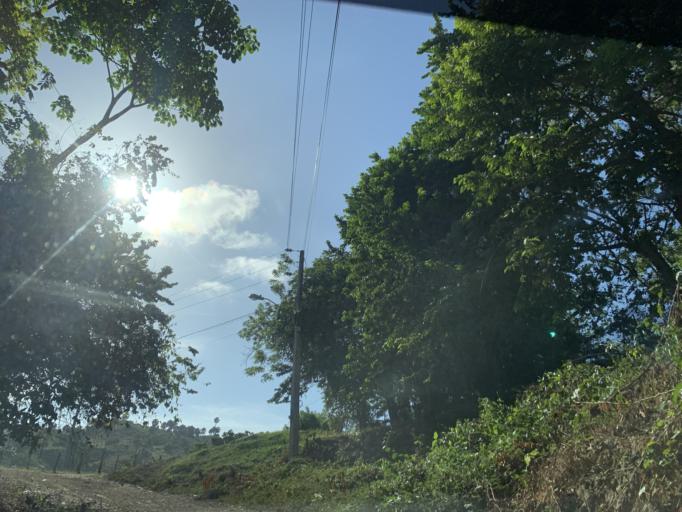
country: DO
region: Puerto Plata
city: Luperon
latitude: 19.8898
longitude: -70.8889
